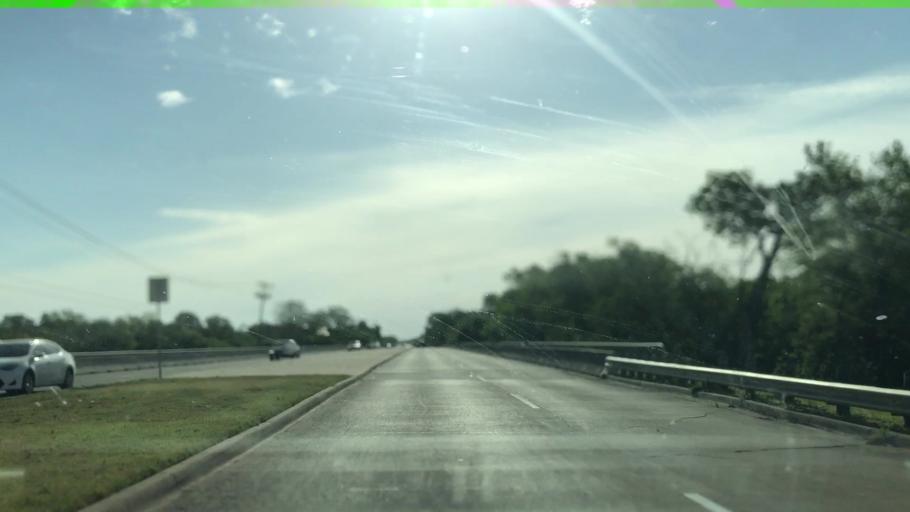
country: US
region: Texas
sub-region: Dallas County
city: Farmers Branch
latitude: 32.8956
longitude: -96.9311
